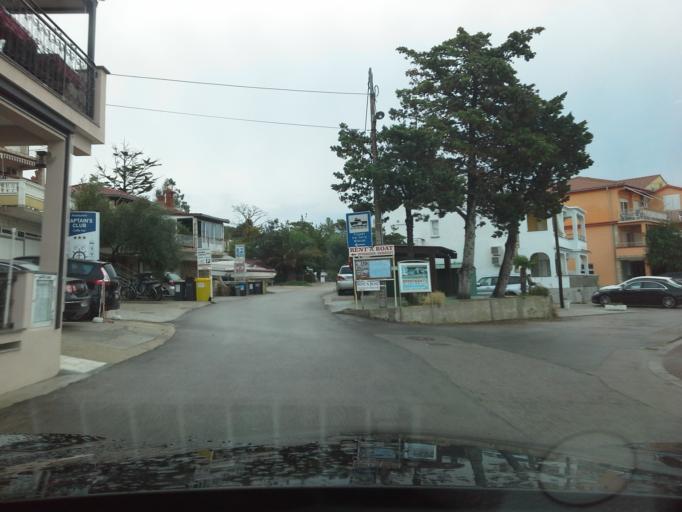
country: HR
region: Primorsko-Goranska
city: Banjol
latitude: 44.7482
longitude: 14.7846
